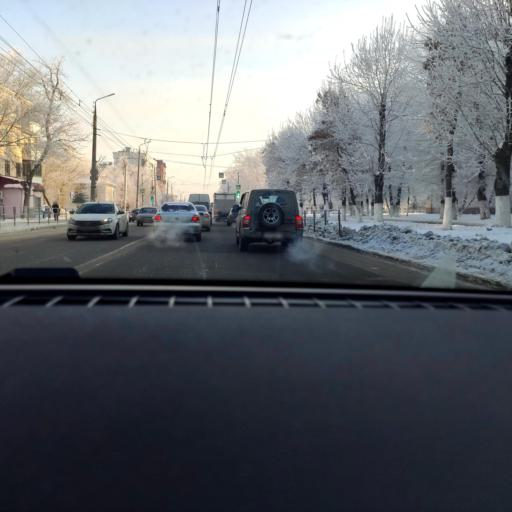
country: RU
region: Samara
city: Novokuybyshevsk
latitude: 53.0950
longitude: 49.9739
